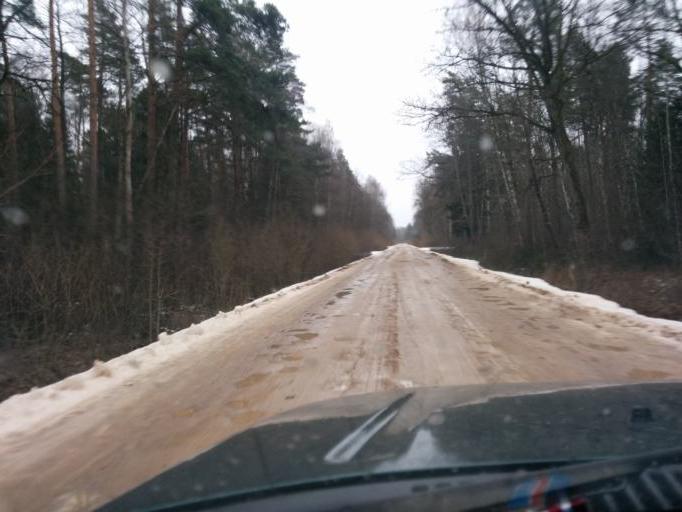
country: LV
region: Ozolnieku
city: Ozolnieki
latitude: 56.6859
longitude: 23.7684
